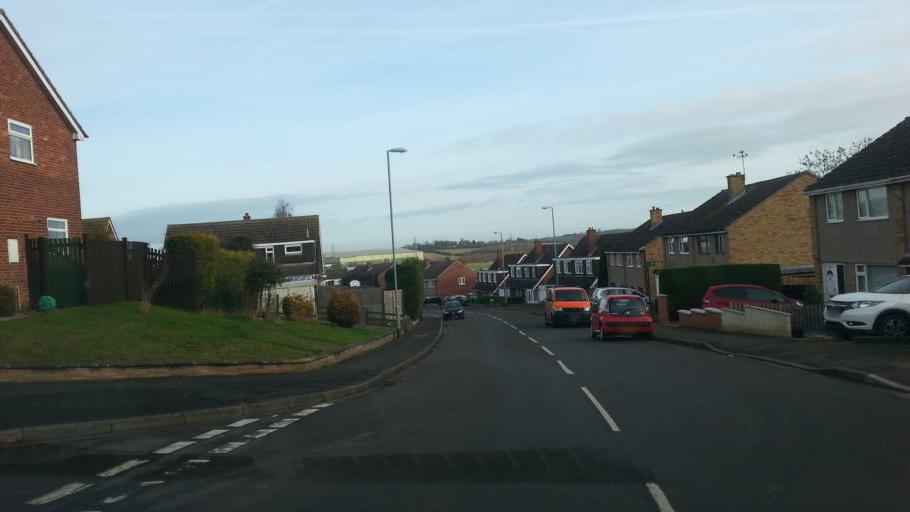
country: GB
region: England
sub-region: Leicestershire
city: Melton Mowbray
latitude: 52.7578
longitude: -0.8689
